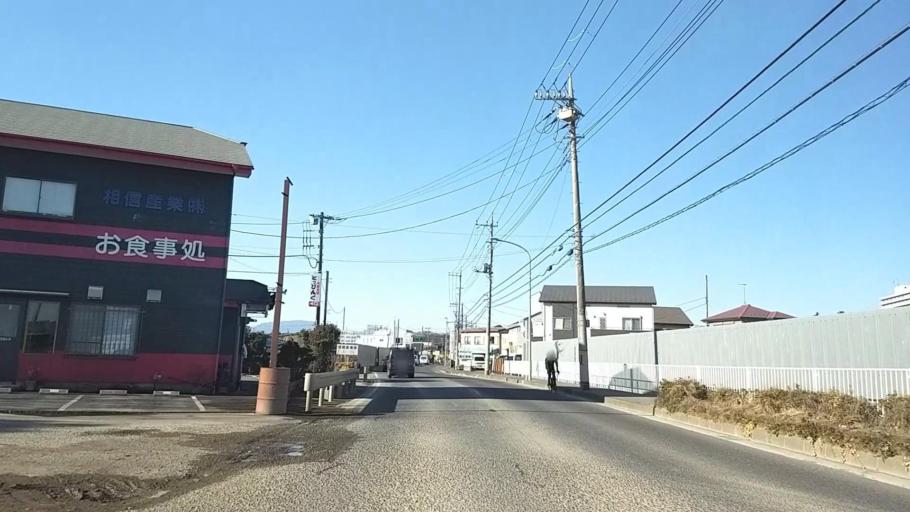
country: JP
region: Kanagawa
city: Isehara
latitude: 35.3592
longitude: 139.2818
